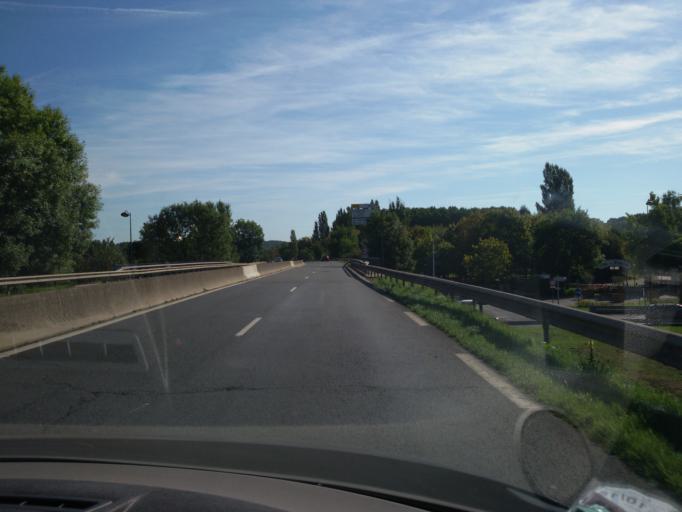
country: FR
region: Ile-de-France
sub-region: Departement de l'Essonne
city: Etampes
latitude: 48.4282
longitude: 2.1581
